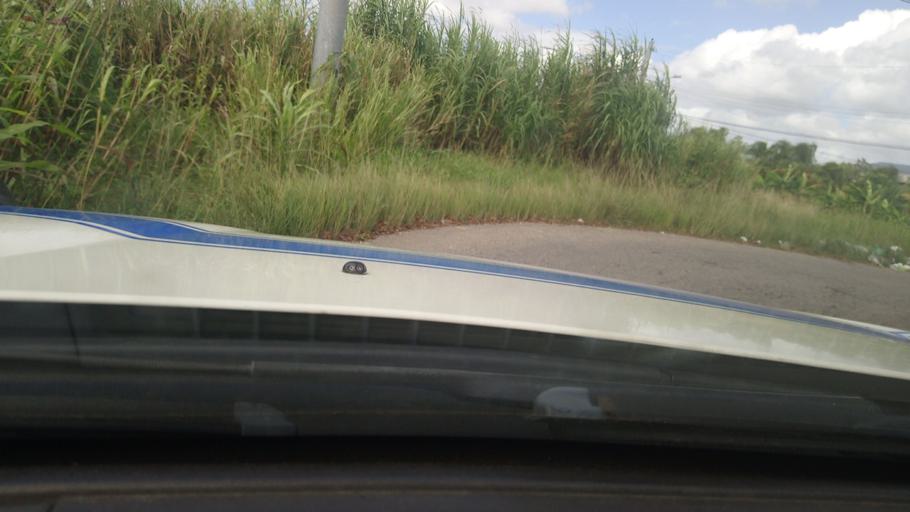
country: TT
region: Borough of Arima
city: Arima
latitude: 10.6204
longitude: -61.3012
